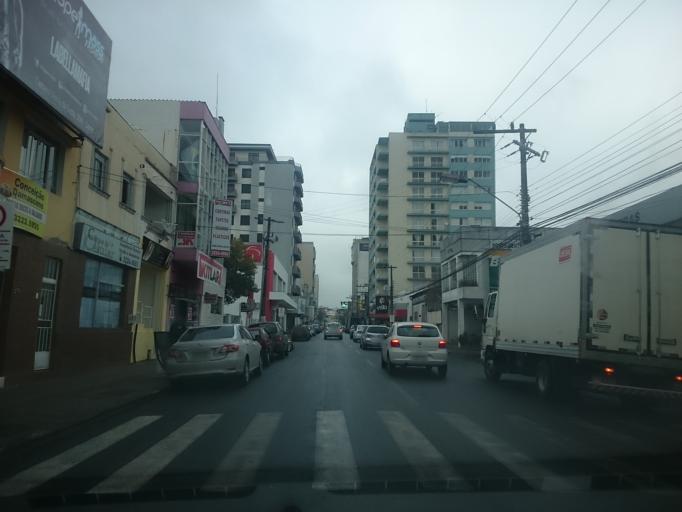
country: BR
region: Santa Catarina
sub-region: Lages
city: Lages
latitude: -27.8127
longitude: -50.3250
